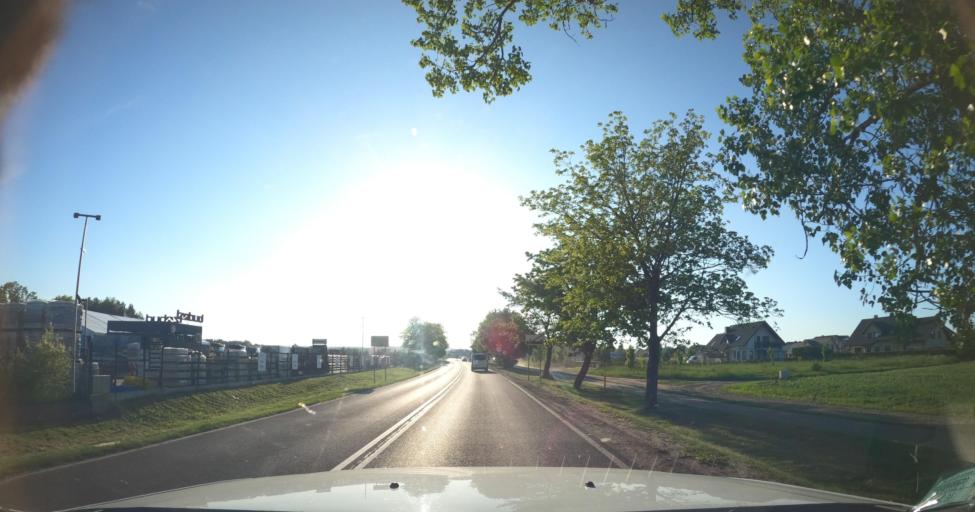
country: PL
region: Pomeranian Voivodeship
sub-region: Powiat kartuski
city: Kartuzy
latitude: 54.3173
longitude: 18.2620
